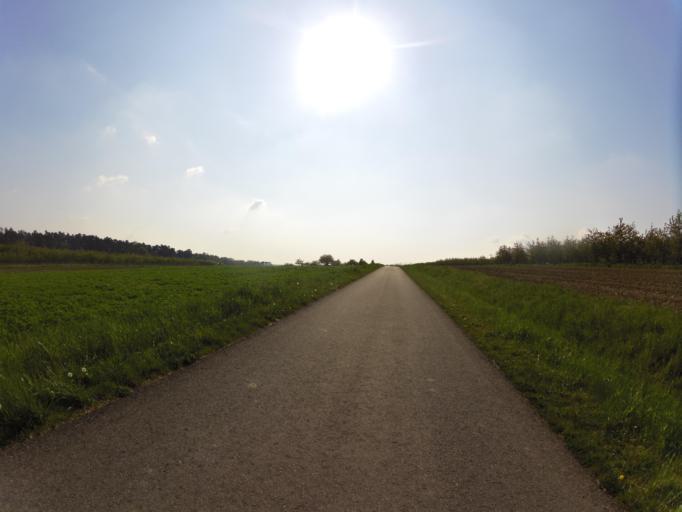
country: DE
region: Bavaria
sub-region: Regierungsbezirk Unterfranken
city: Sommerhausen
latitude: 49.7088
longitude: 10.0495
